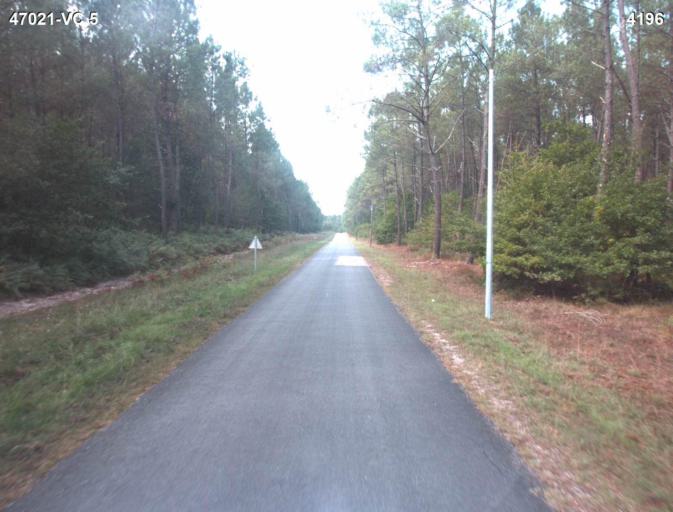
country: FR
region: Aquitaine
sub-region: Departement du Lot-et-Garonne
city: Barbaste
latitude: 44.1441
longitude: 0.2474
